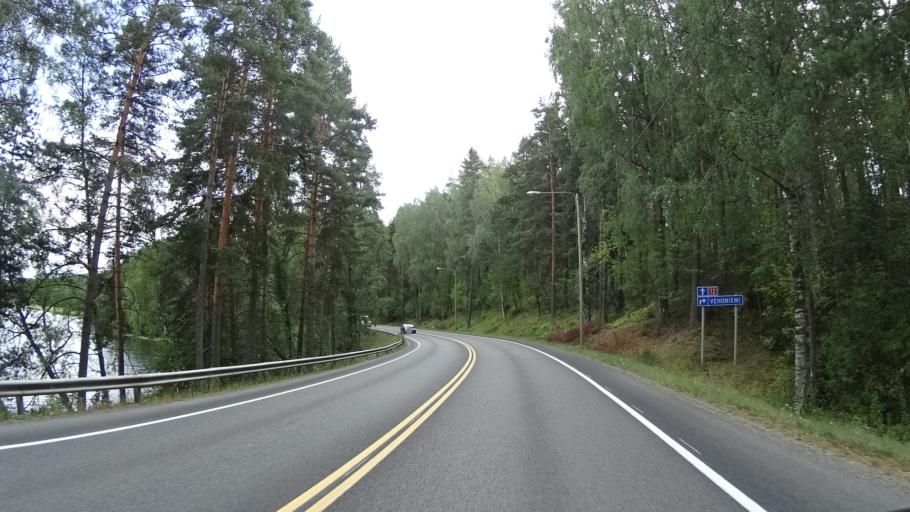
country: FI
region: Pirkanmaa
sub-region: Tampere
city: Kangasala
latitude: 61.4160
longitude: 24.1467
